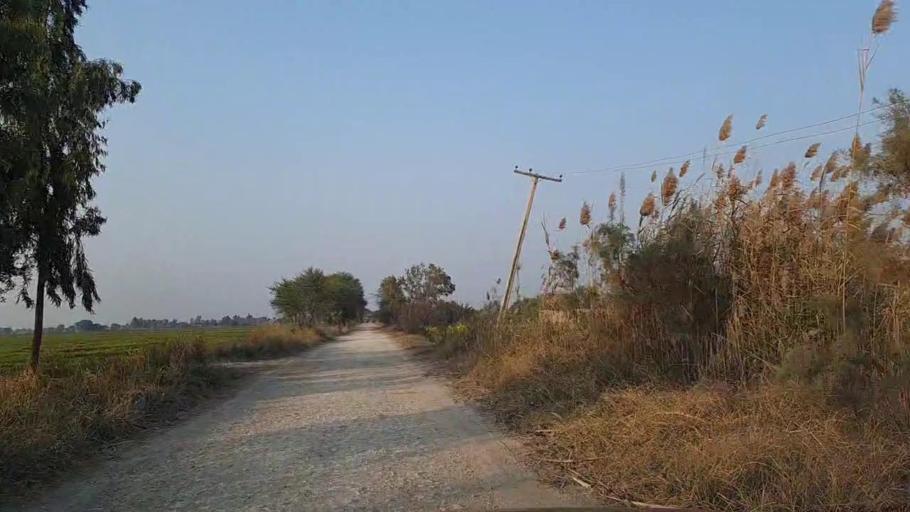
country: PK
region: Sindh
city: Daur
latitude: 26.4298
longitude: 68.3937
